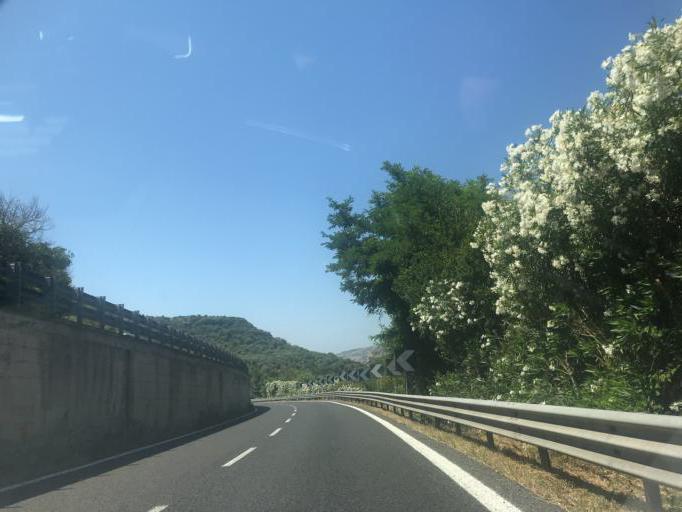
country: IT
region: Sardinia
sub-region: Provincia di Sassari
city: Codrongianos
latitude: 40.6525
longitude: 8.6735
